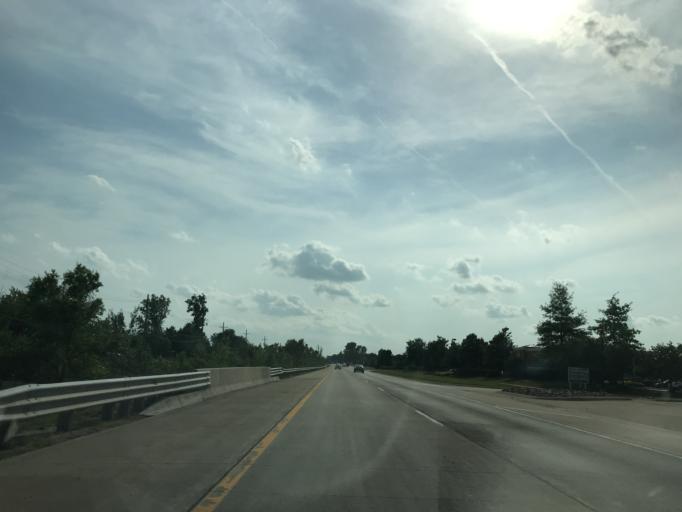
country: US
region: Michigan
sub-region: Wayne County
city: Canton
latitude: 42.2691
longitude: -83.4981
